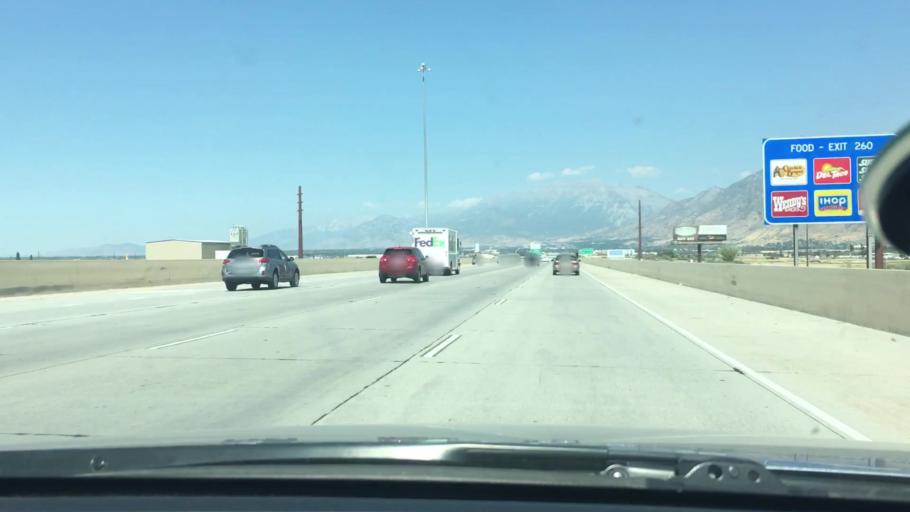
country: US
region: Utah
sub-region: Utah County
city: Spanish Fork
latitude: 40.1355
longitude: -111.6466
